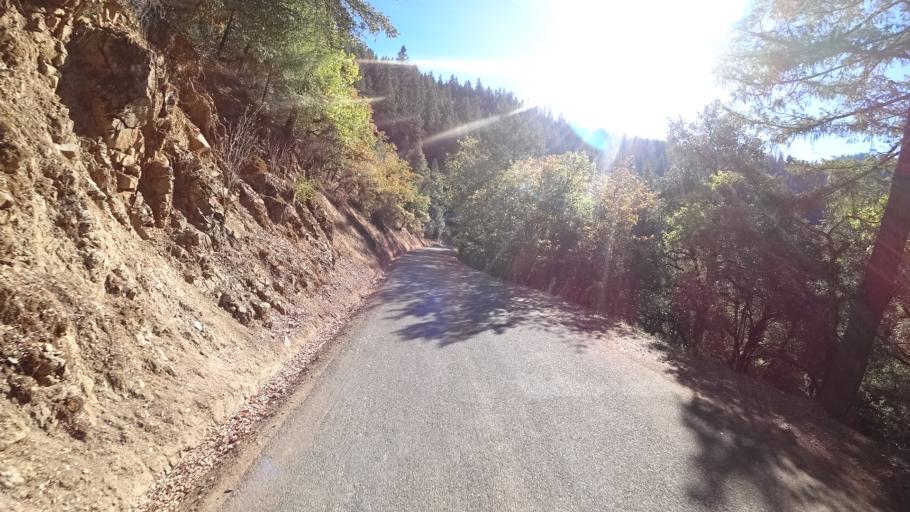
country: US
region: California
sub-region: Humboldt County
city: Willow Creek
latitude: 41.2537
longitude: -123.3102
